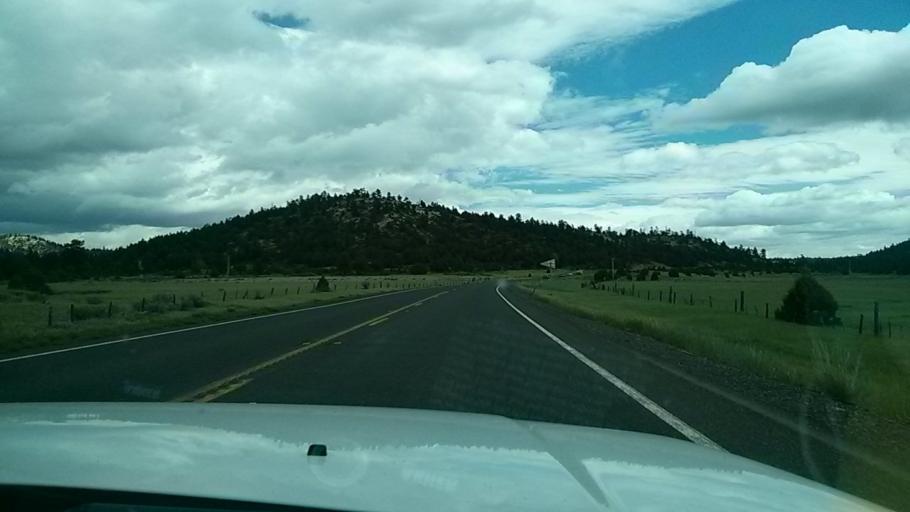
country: US
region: Utah
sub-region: Garfield County
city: Panguitch
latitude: 37.4418
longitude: -112.5377
